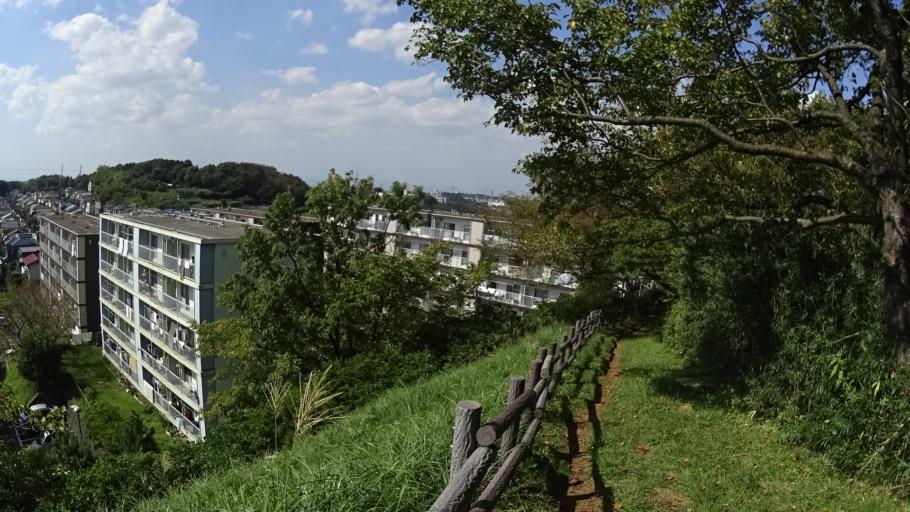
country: JP
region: Kanagawa
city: Kamakura
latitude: 35.3607
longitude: 139.5848
